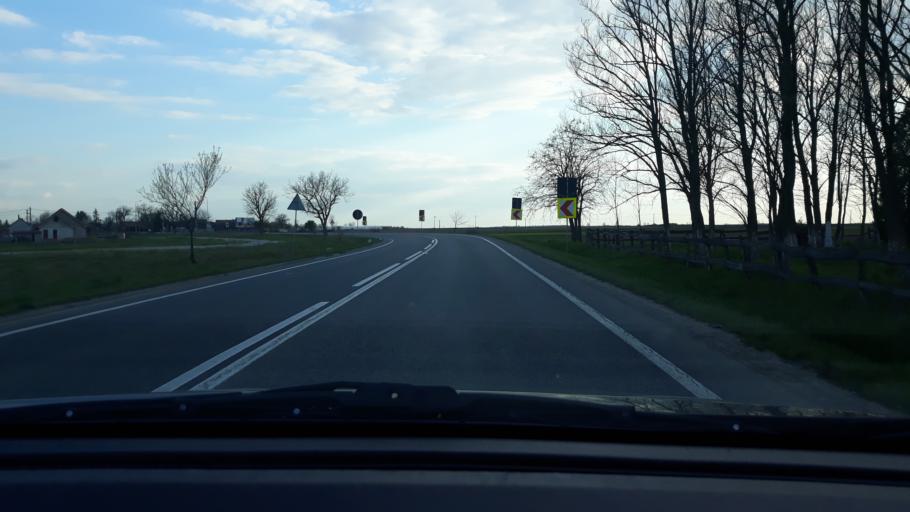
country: RO
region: Bihor
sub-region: Comuna Tamaseu
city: Tamaseu
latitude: 47.2047
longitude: 21.9205
